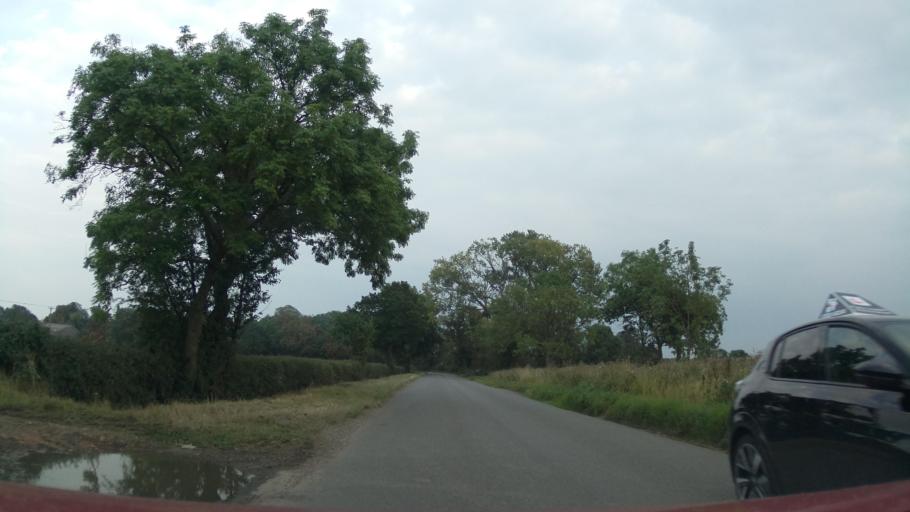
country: GB
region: England
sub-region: Lincolnshire
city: Skellingthorpe
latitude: 53.1429
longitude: -0.6509
